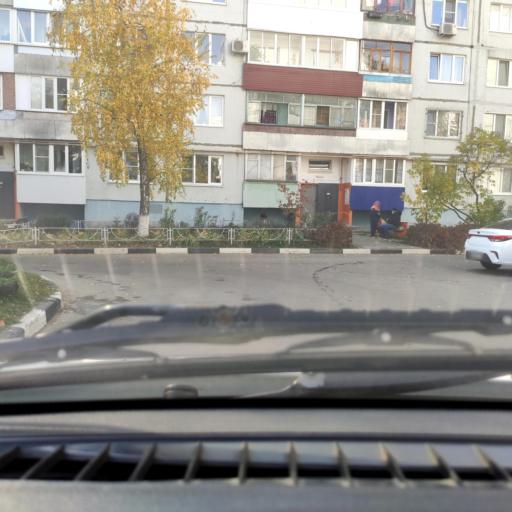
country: RU
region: Samara
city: Zhigulevsk
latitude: 53.4842
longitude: 49.4642
